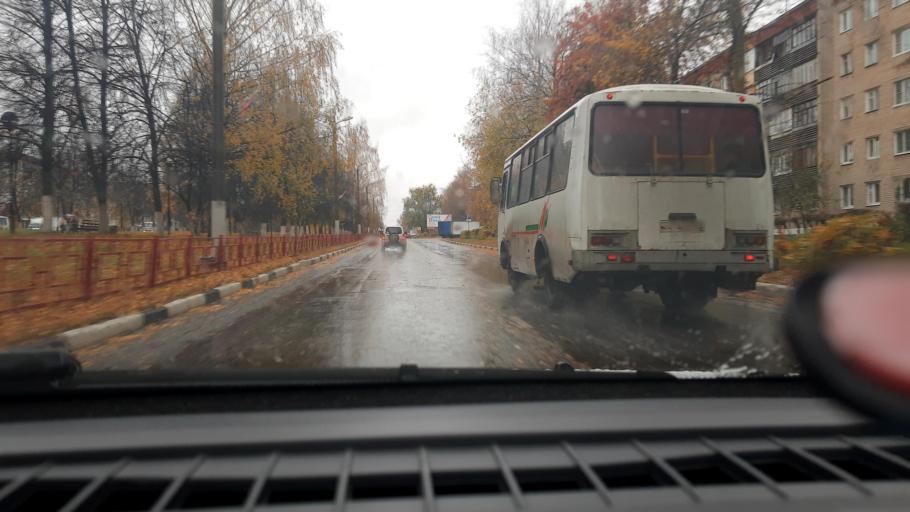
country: RU
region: Nizjnij Novgorod
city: Kstovo
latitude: 56.1444
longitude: 44.1930
